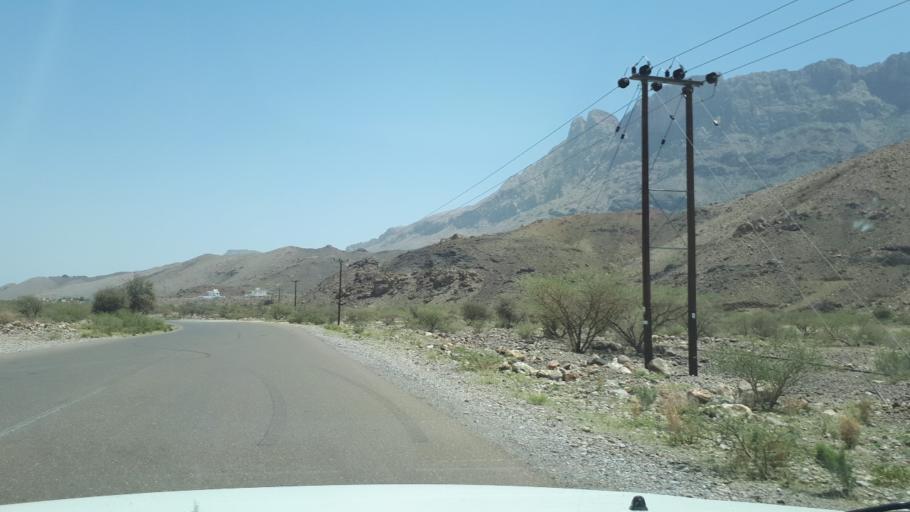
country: OM
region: Muhafazat ad Dakhiliyah
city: Bahla'
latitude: 23.1602
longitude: 57.1680
